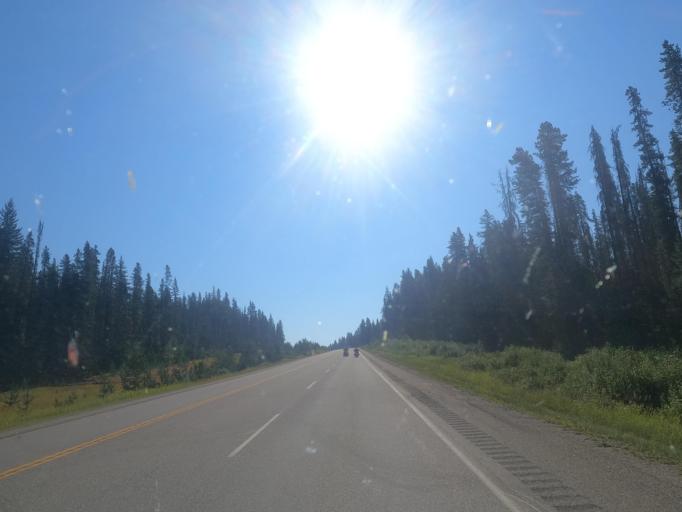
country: CA
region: Alberta
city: Grande Cache
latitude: 53.0054
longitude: -119.0535
